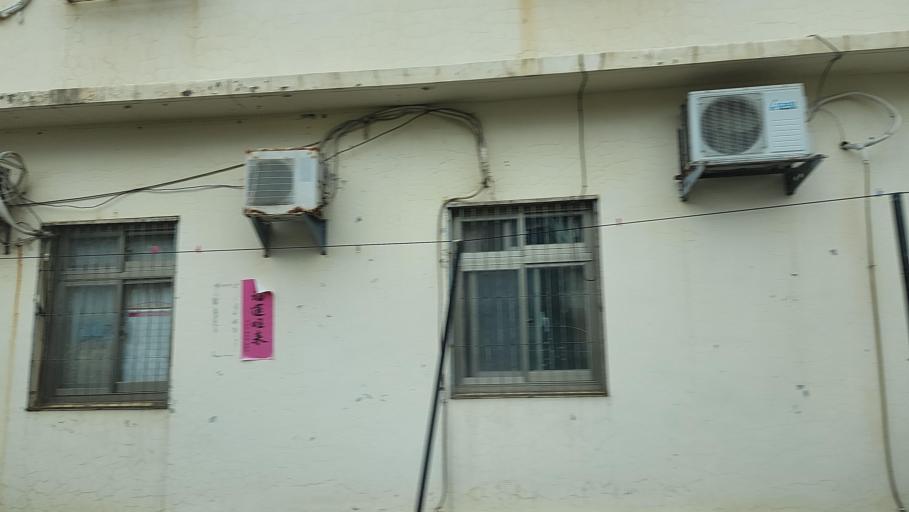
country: TW
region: Taiwan
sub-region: Keelung
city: Keelung
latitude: 25.2108
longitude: 121.6567
